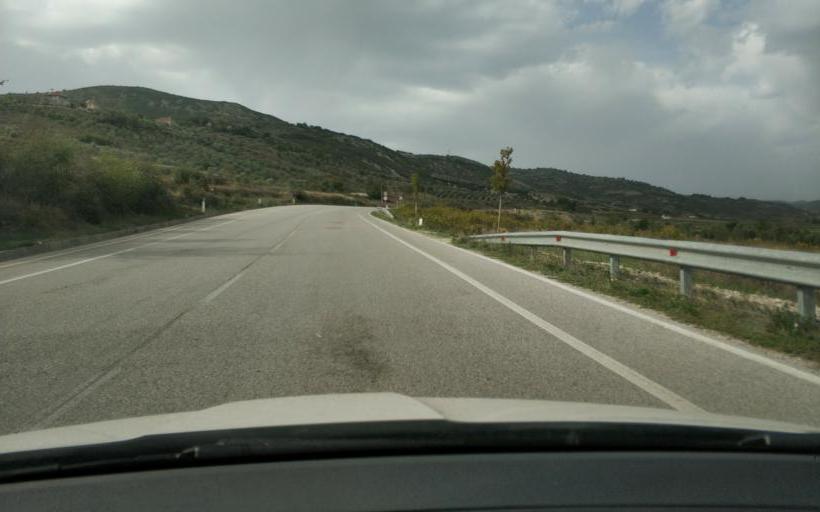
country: AL
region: Gjirokaster
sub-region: Rrethi i Tepelenes
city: Krahes
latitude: 40.4386
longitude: 19.8499
